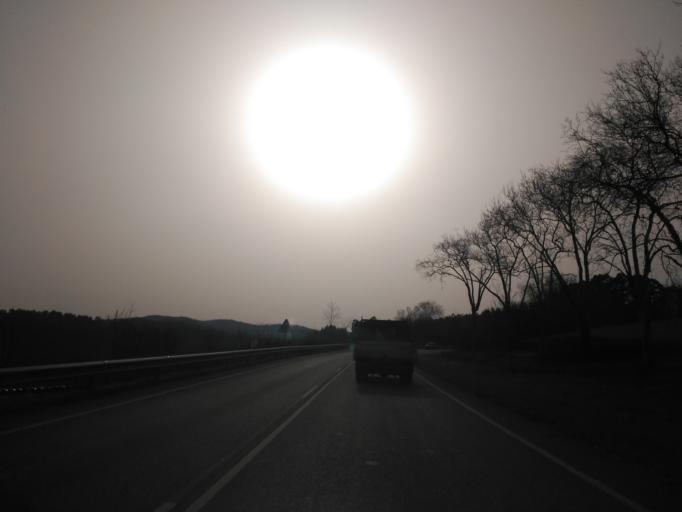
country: ES
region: Cantabria
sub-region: Provincia de Cantabria
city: Comillas
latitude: 43.3736
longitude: -4.2832
